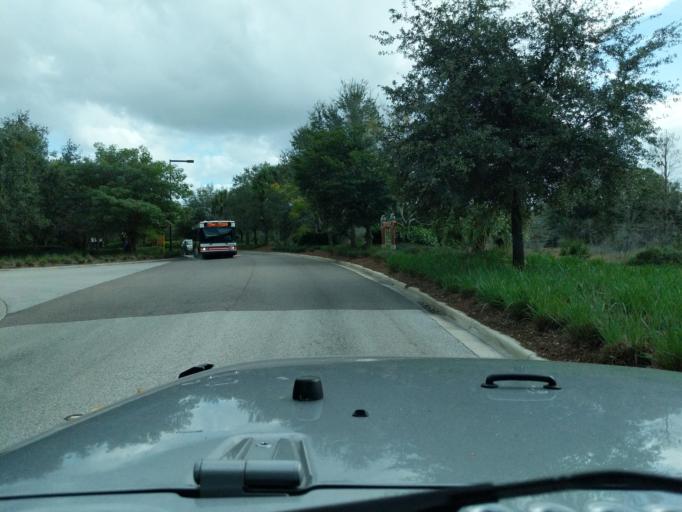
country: US
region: Florida
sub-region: Polk County
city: Citrus Ridge
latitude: 28.3506
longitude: -81.6064
